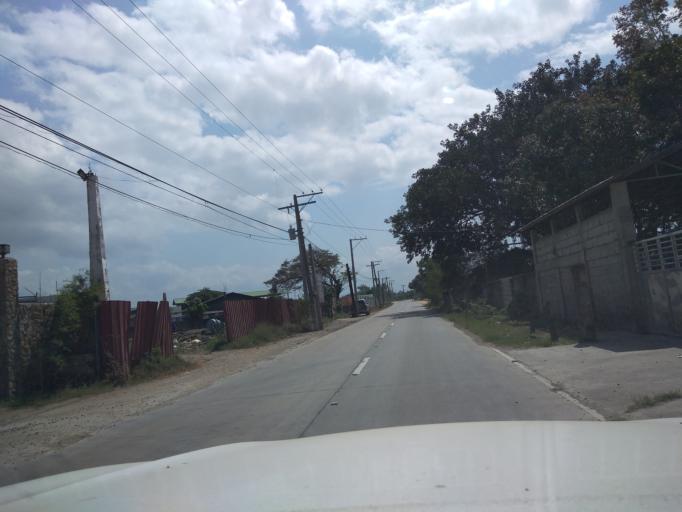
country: PH
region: Central Luzon
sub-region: Province of Pampanga
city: Talang
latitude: 15.0241
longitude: 120.8431
